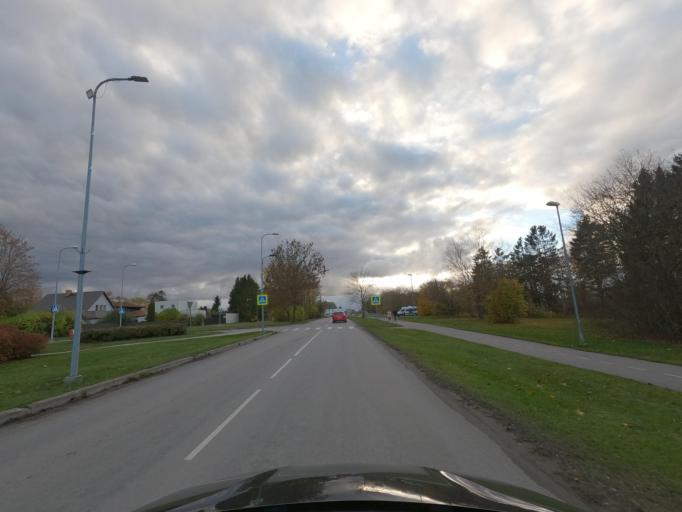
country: EE
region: Harju
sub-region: Saue linn
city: Saue
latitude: 59.3255
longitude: 24.5522
